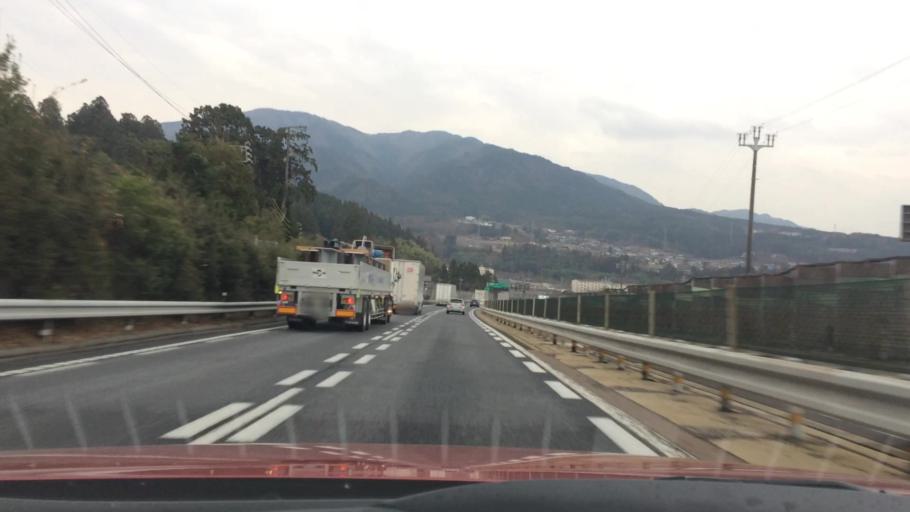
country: JP
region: Gifu
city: Nakatsugawa
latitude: 35.4835
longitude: 137.5104
